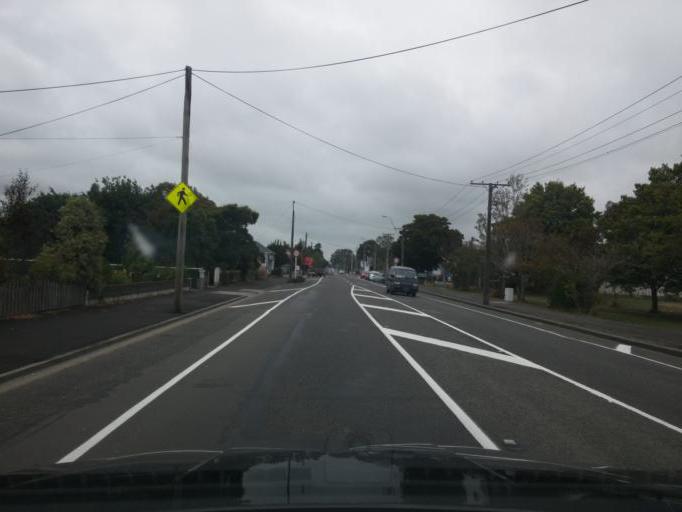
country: NZ
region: Wellington
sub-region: Masterton District
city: Masterton
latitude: -41.0890
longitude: 175.4508
